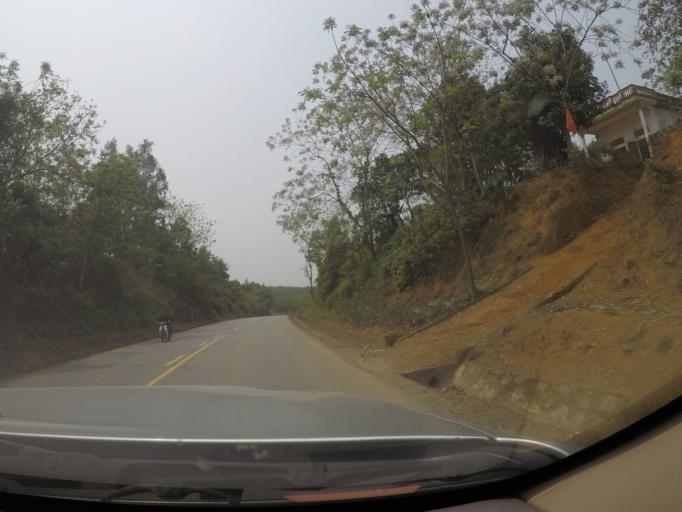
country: VN
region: Thanh Hoa
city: Thi Tran Ngoc Lac
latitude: 20.1381
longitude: 105.4213
